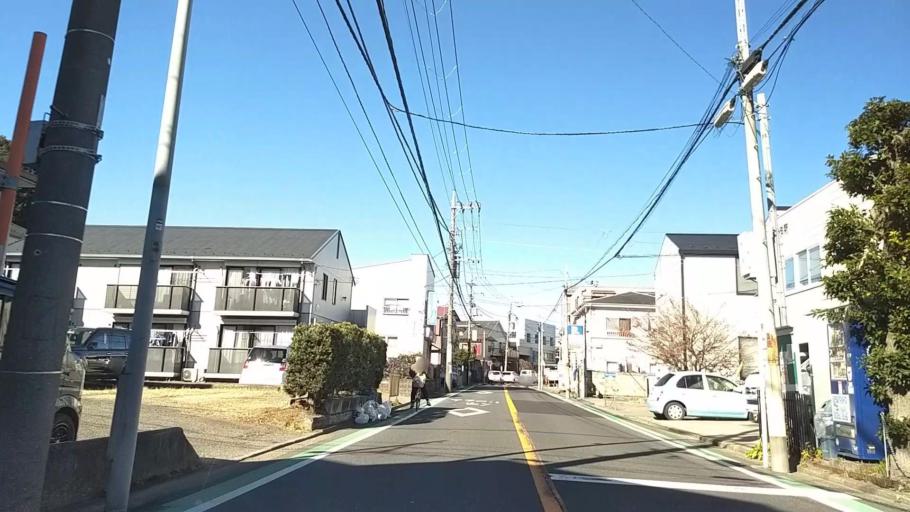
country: JP
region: Kanagawa
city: Yokohama
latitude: 35.4595
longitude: 139.5907
